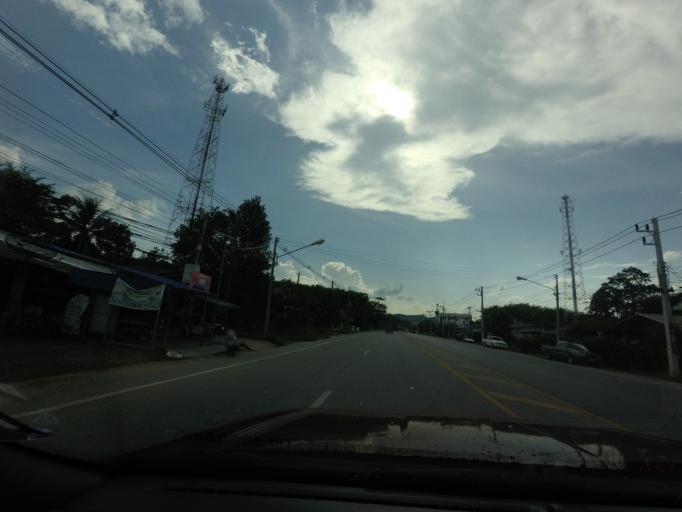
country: TH
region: Pattani
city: Khok Pho
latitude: 6.6755
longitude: 101.1503
